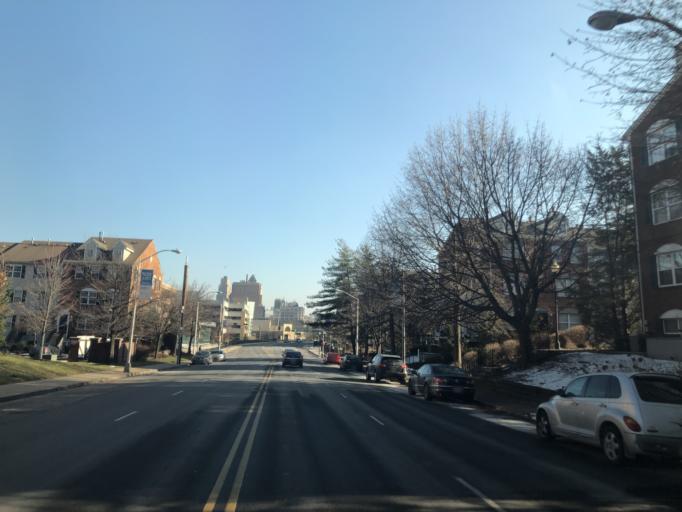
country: US
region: New Jersey
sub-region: Essex County
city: Newark
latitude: 40.7404
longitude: -74.1837
